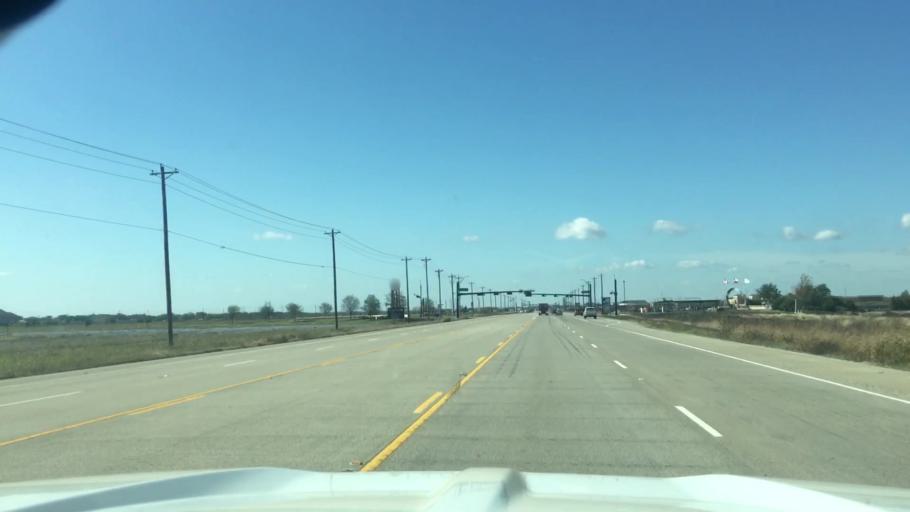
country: US
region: Texas
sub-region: Collin County
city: Prosper
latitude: 33.2192
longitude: -96.8700
